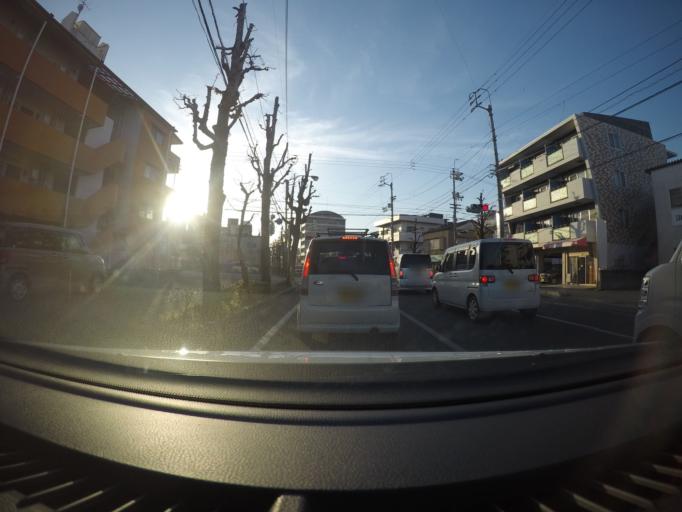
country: JP
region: Kochi
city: Kochi-shi
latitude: 33.5563
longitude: 133.5563
